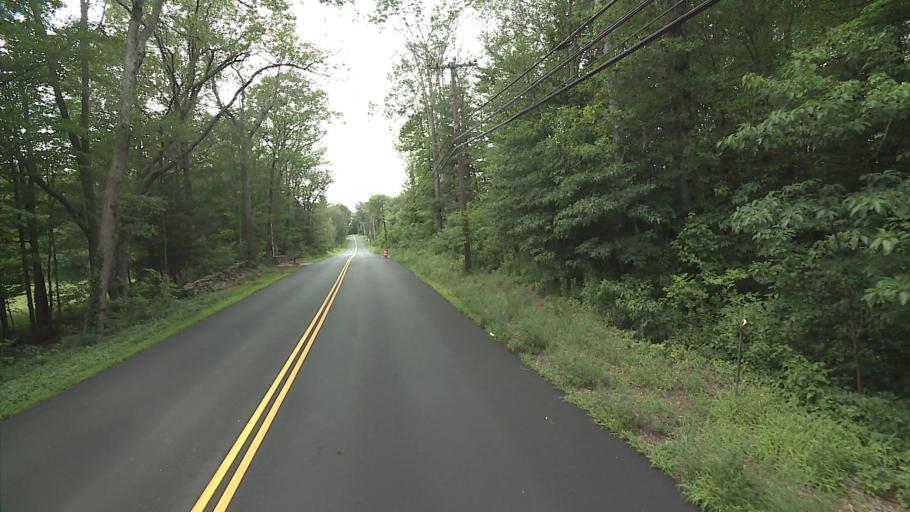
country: US
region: Connecticut
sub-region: Windham County
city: South Woodstock
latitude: 41.9537
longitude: -72.0512
